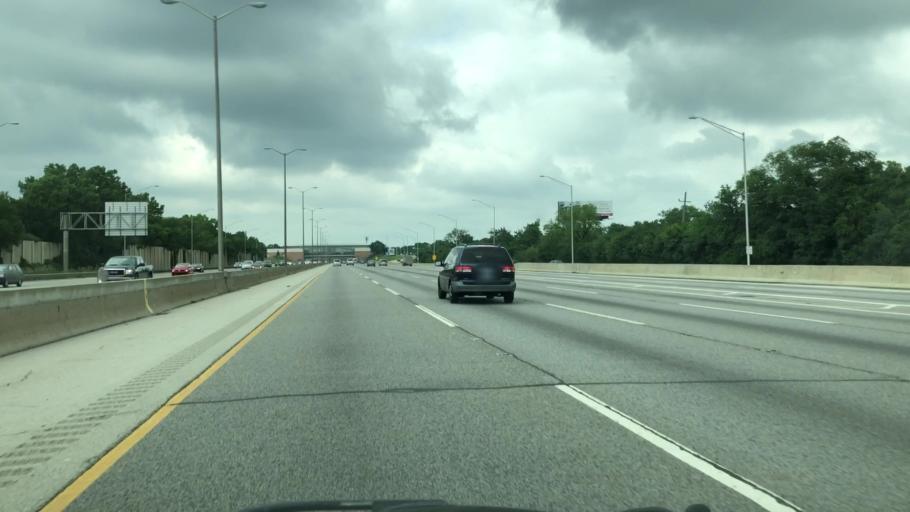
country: US
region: Illinois
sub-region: Cook County
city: Indian Head Park
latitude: 41.7771
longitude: -87.9077
